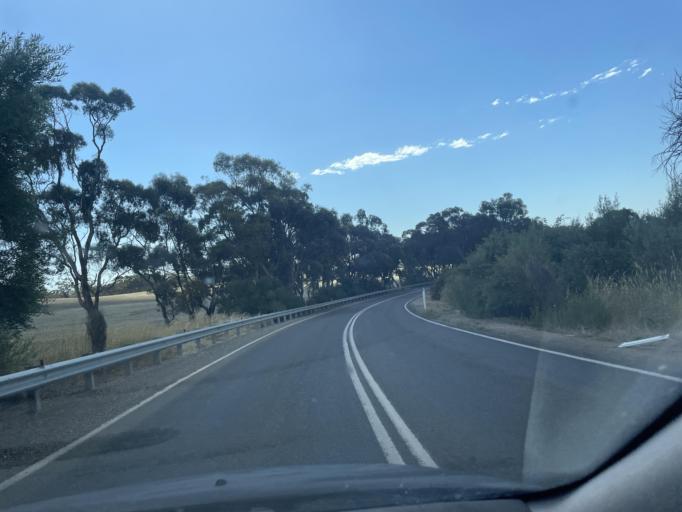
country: AU
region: South Australia
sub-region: Clare and Gilbert Valleys
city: Clare
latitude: -33.9044
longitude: 138.6952
